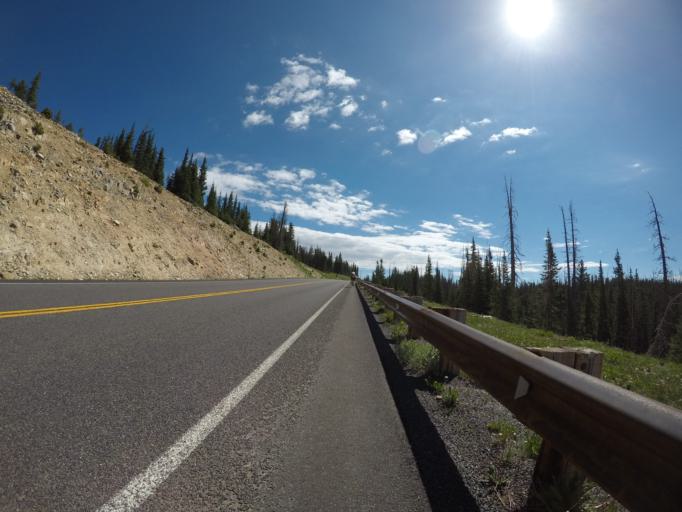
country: US
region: Wyoming
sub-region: Carbon County
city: Saratoga
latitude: 41.3133
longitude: -106.3543
